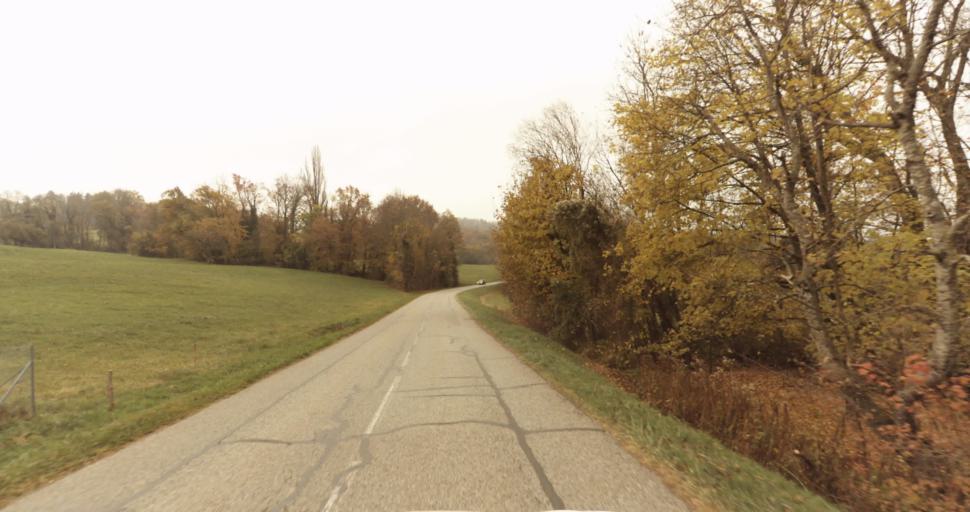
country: FR
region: Rhone-Alpes
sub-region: Departement de la Haute-Savoie
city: Saint-Felix
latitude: 45.7983
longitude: 5.9935
